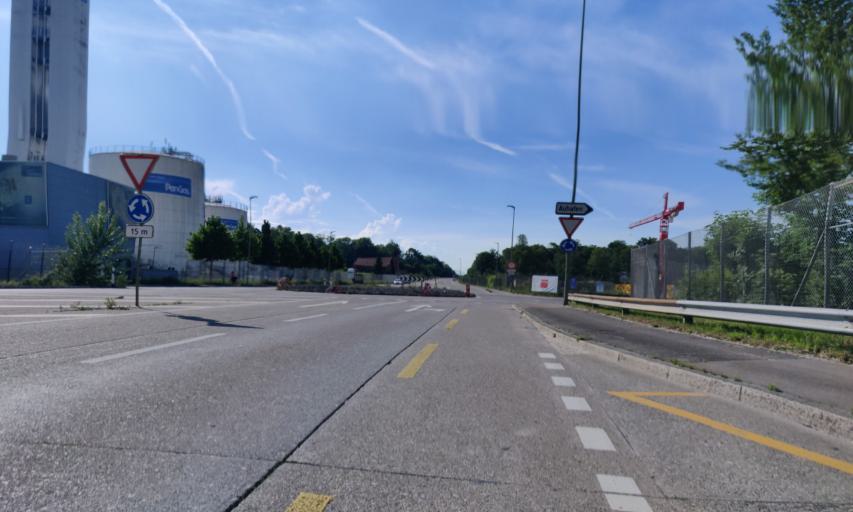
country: CH
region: Basel-Landschaft
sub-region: Bezirk Arlesheim
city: Muttenz
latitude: 47.5369
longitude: 7.6613
